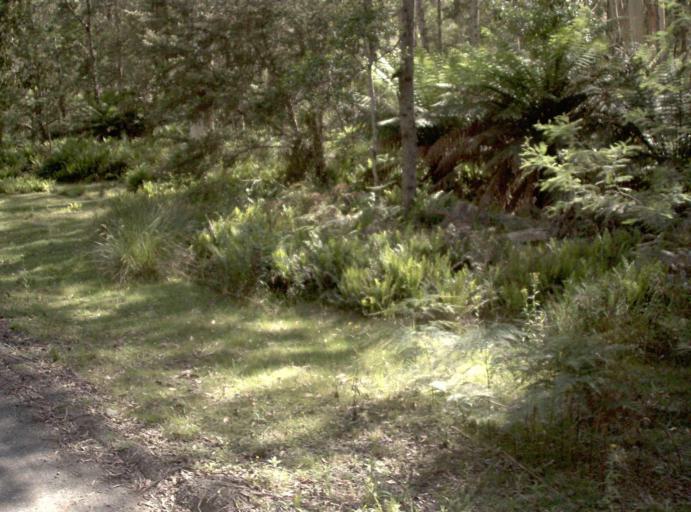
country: AU
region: New South Wales
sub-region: Bombala
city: Bombala
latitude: -37.2140
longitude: 148.7457
